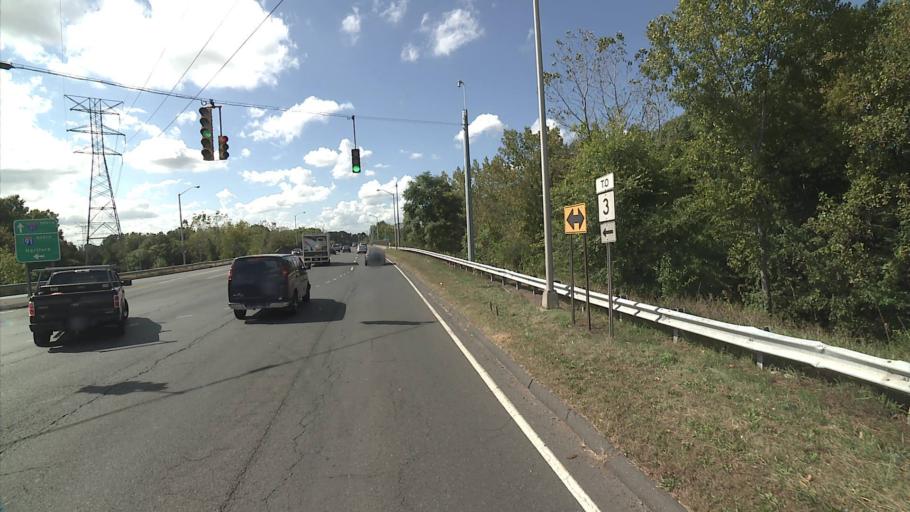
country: US
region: Connecticut
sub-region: Middlesex County
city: Cromwell
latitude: 41.6510
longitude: -72.6706
